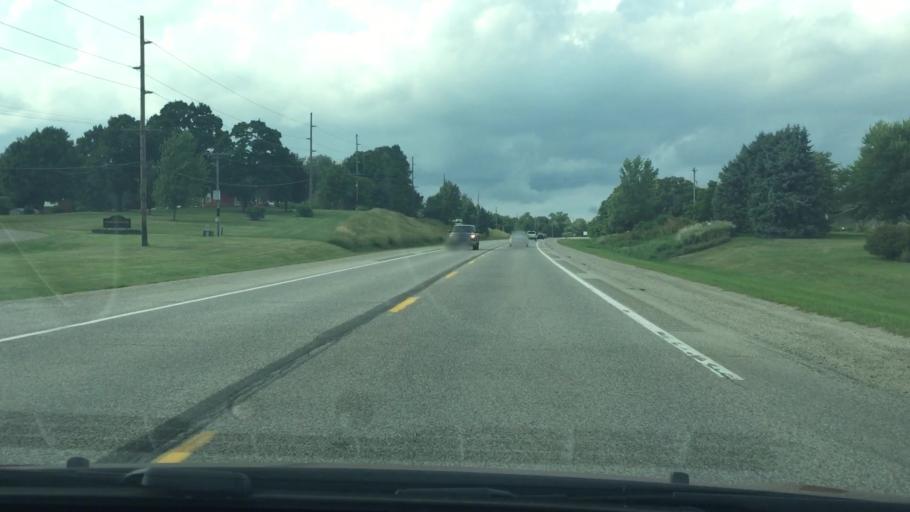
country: US
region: Iowa
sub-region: Muscatine County
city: Muscatine
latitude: 41.4702
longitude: -91.0365
